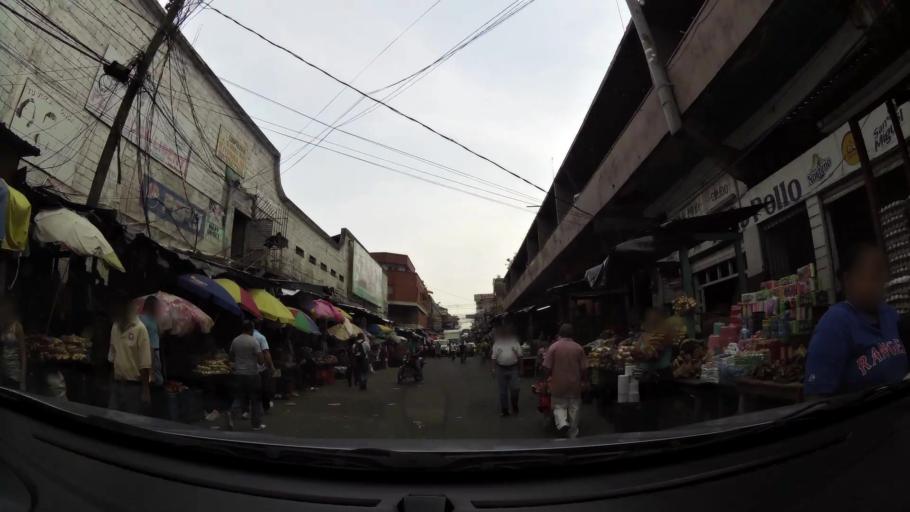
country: HN
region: Francisco Morazan
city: Tegucigalpa
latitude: 14.1021
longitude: -87.2096
